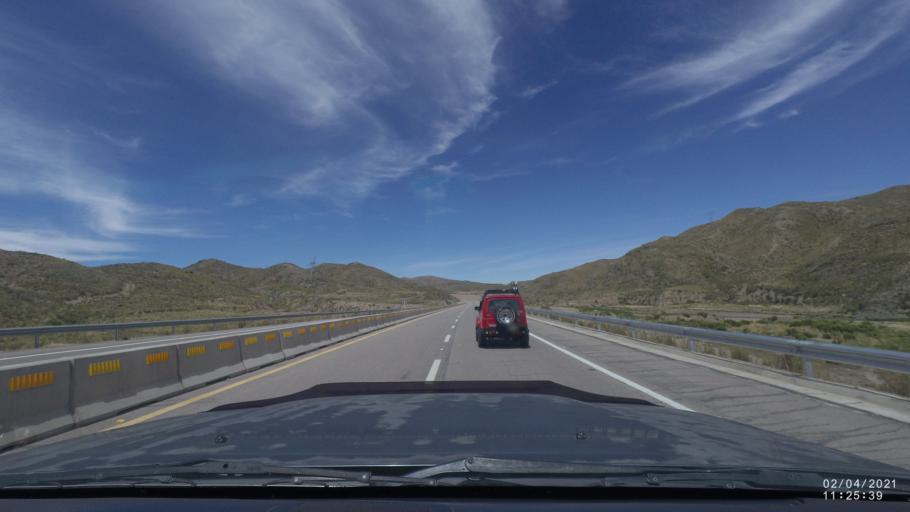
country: BO
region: La Paz
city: Colquiri
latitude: -17.6526
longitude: -66.9854
